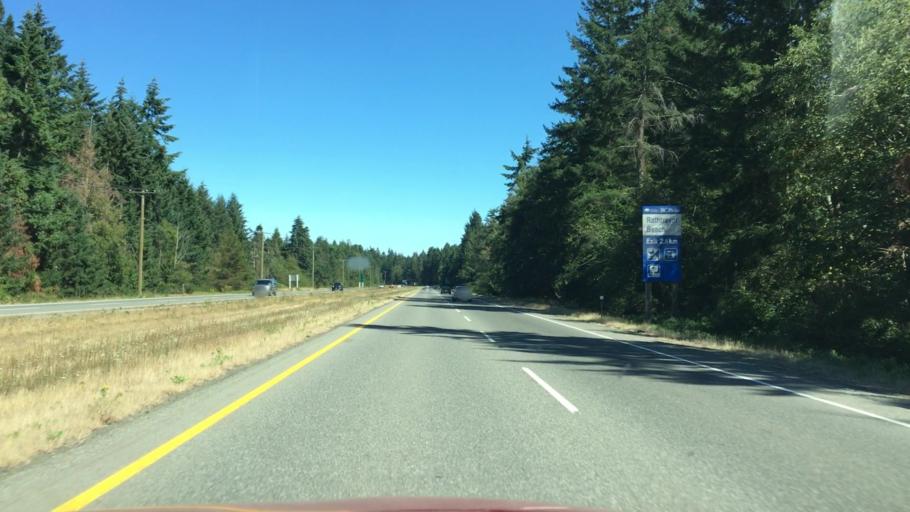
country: CA
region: British Columbia
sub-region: Regional District of Nanaimo
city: Parksville
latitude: 49.3001
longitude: -124.2916
